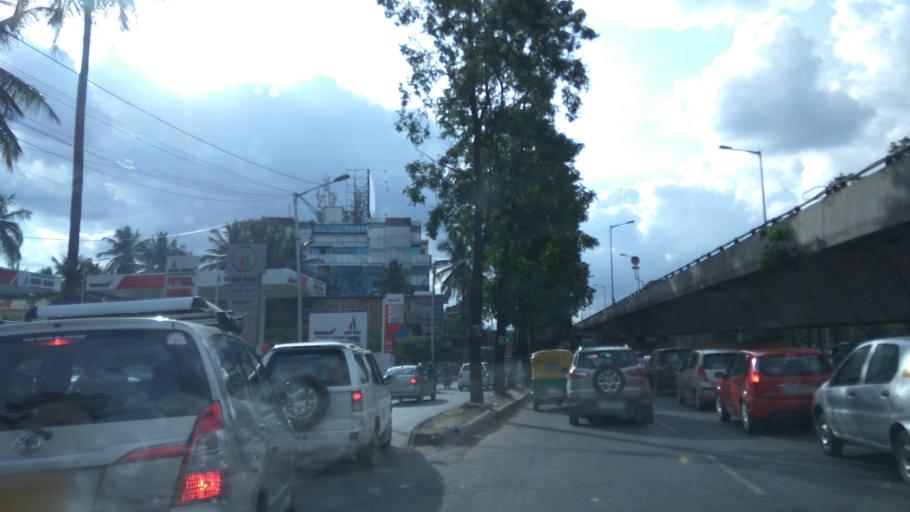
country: IN
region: Karnataka
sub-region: Bangalore Urban
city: Yelahanka
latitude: 13.0423
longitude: 77.5926
